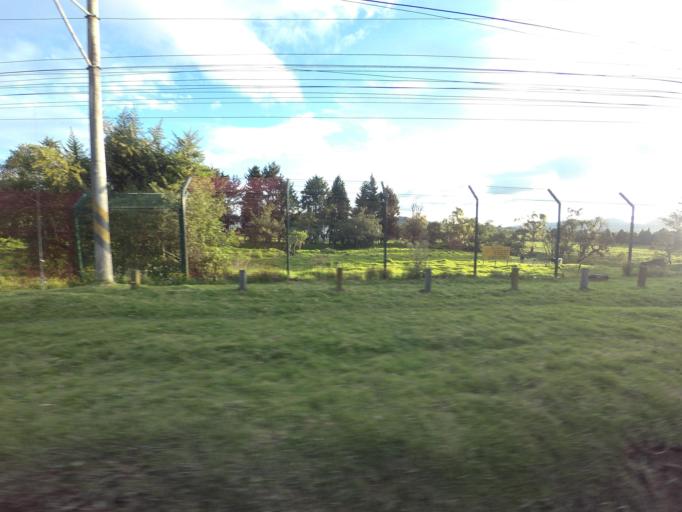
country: CO
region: Cundinamarca
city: Cota
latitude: 4.7922
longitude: -74.0291
